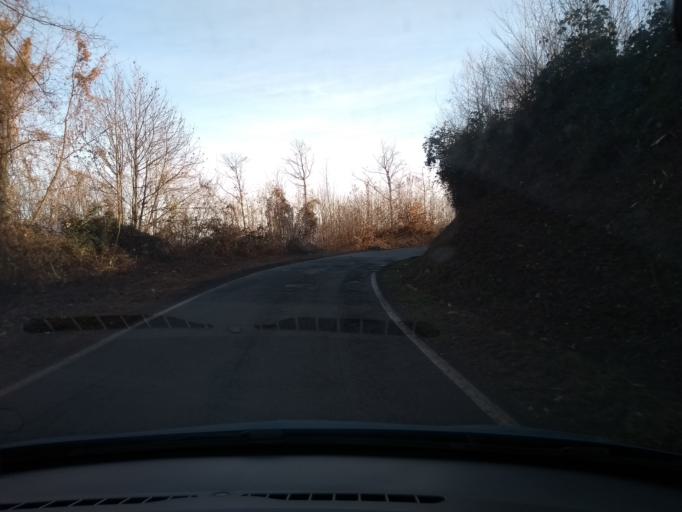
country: IT
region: Piedmont
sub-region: Provincia di Torino
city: Rocca Canavese
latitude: 45.2815
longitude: 7.5889
